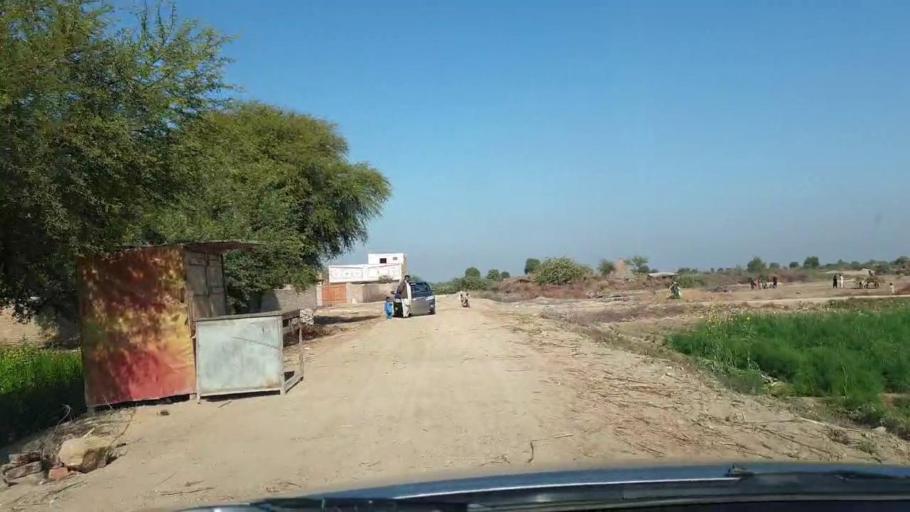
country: PK
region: Sindh
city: Jhol
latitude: 25.8839
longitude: 68.9184
